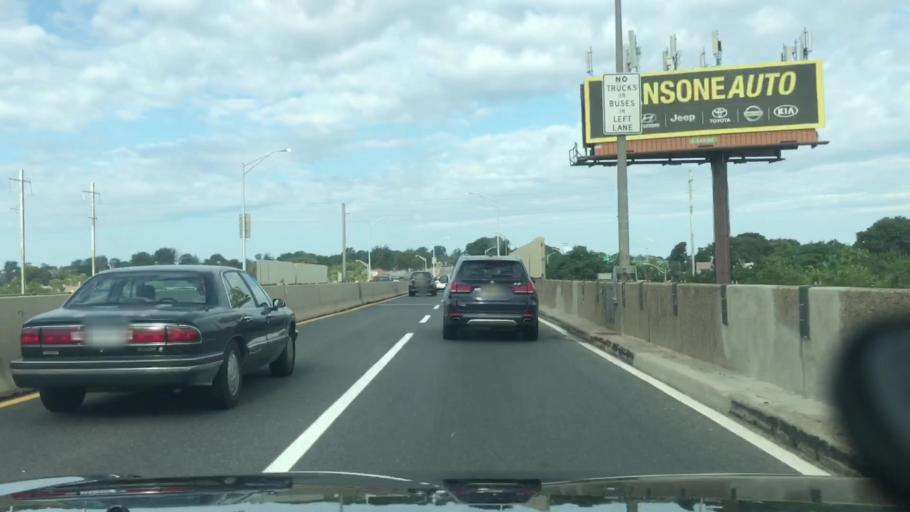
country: US
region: New Jersey
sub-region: Middlesex County
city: Perth Amboy
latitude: 40.5253
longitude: -74.2654
